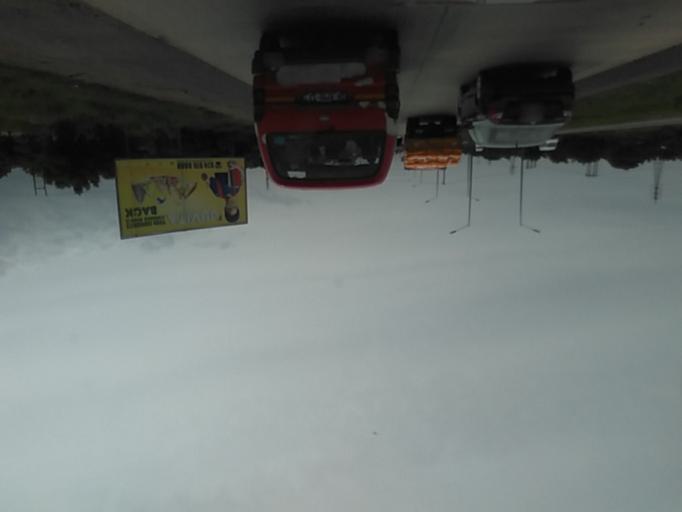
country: GH
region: Greater Accra
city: Nungua
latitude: 5.6553
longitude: -0.0931
